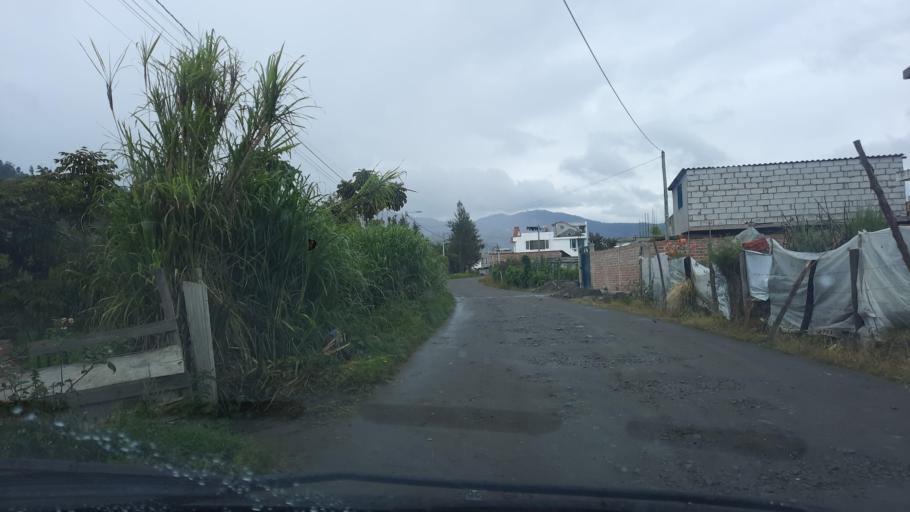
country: EC
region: Chimborazo
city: Riobamba
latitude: -1.6900
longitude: -78.6582
